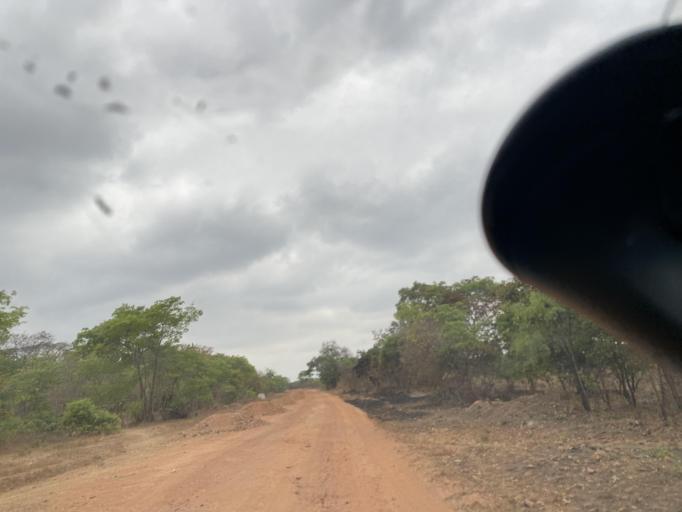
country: ZM
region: Lusaka
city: Chongwe
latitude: -15.2257
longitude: 28.7366
